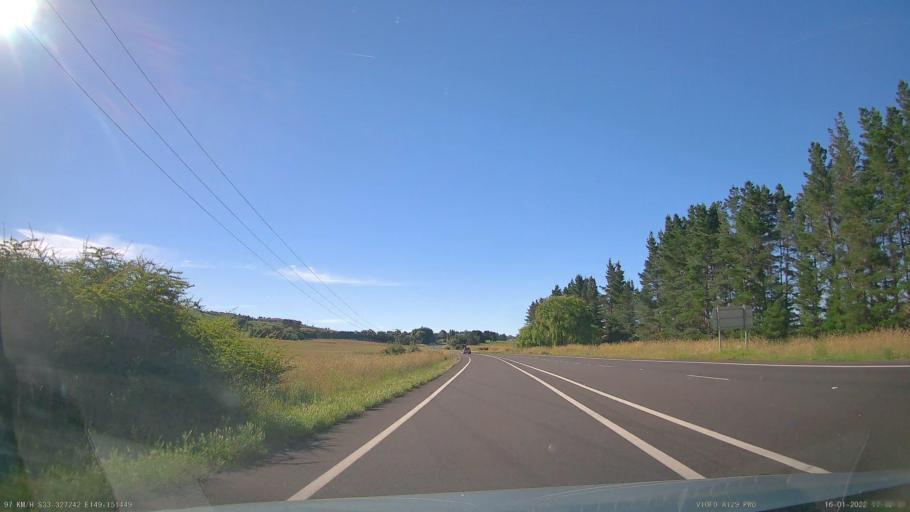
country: AU
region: New South Wales
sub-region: Orange Municipality
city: Orange
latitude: -33.3270
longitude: 149.1513
